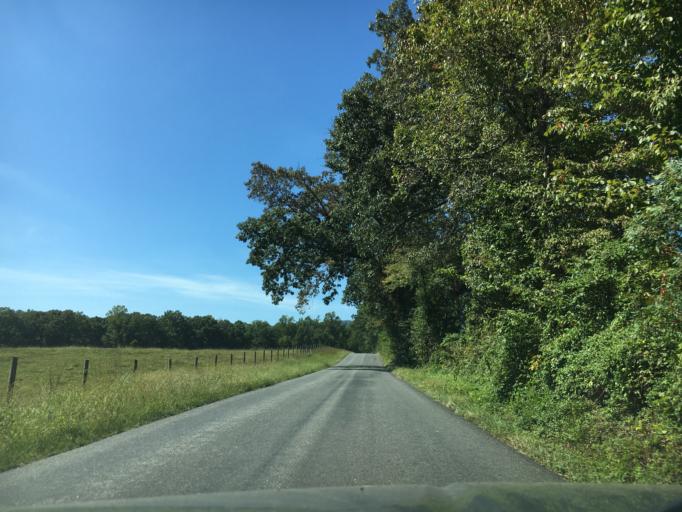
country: US
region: Virginia
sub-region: Albemarle County
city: Crozet
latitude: 38.0207
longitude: -78.7769
